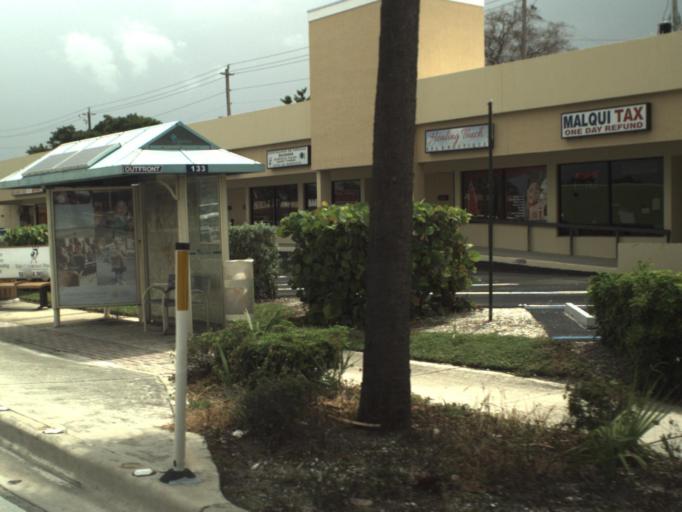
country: US
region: Florida
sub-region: Palm Beach County
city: Lake Clarke Shores
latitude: 26.6609
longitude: -80.0559
